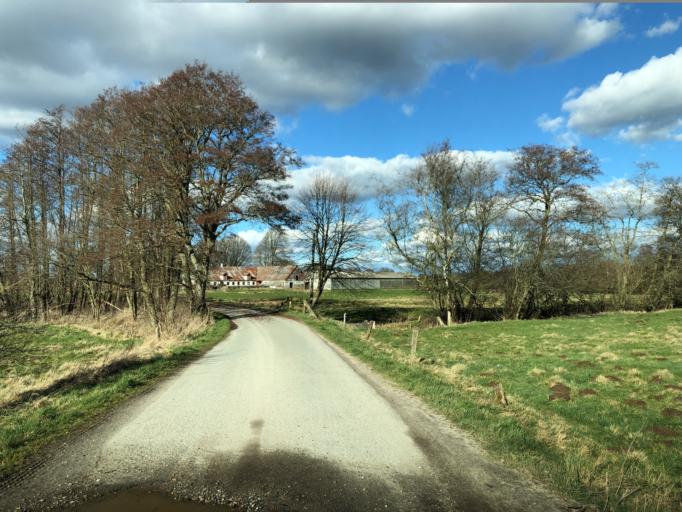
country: DK
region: Central Jutland
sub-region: Randers Kommune
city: Langa
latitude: 56.3234
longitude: 9.9134
